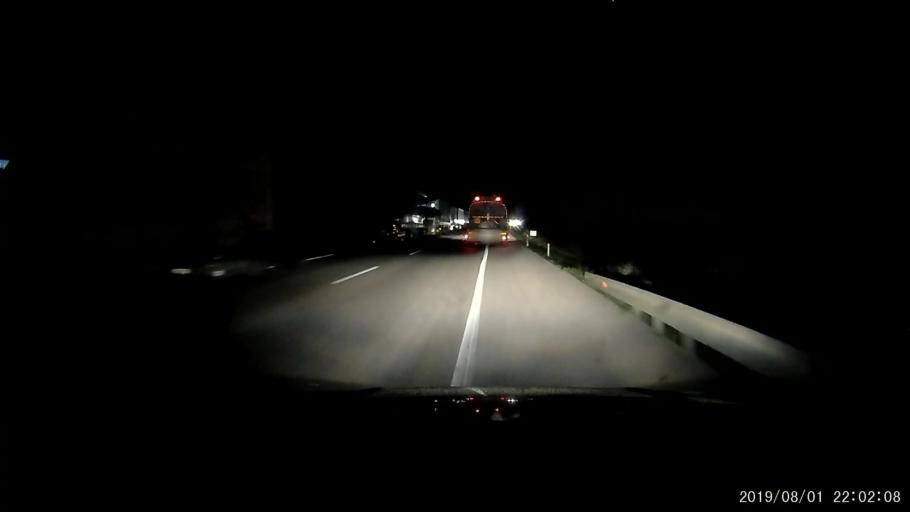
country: TR
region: Edirne
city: Lalapasa
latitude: 41.9316
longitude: 26.6626
